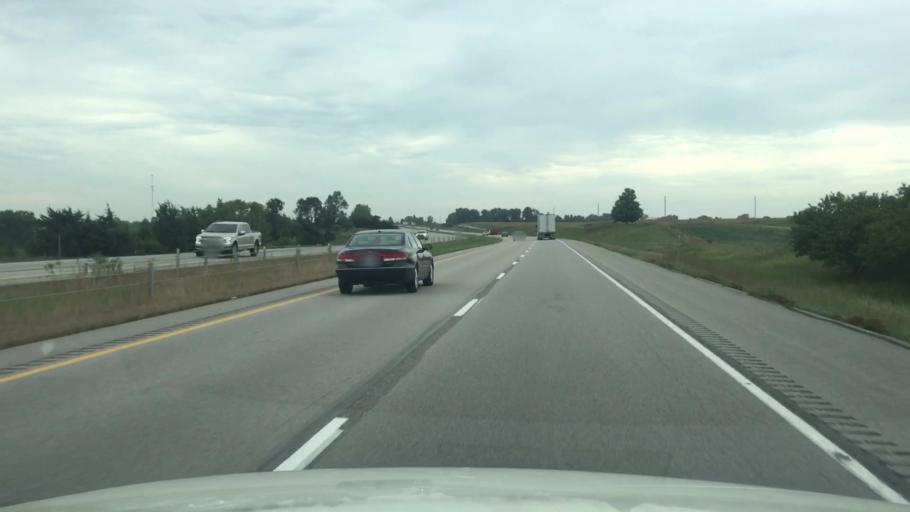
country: US
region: Iowa
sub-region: Clarke County
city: Osceola
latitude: 41.1498
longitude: -93.7878
